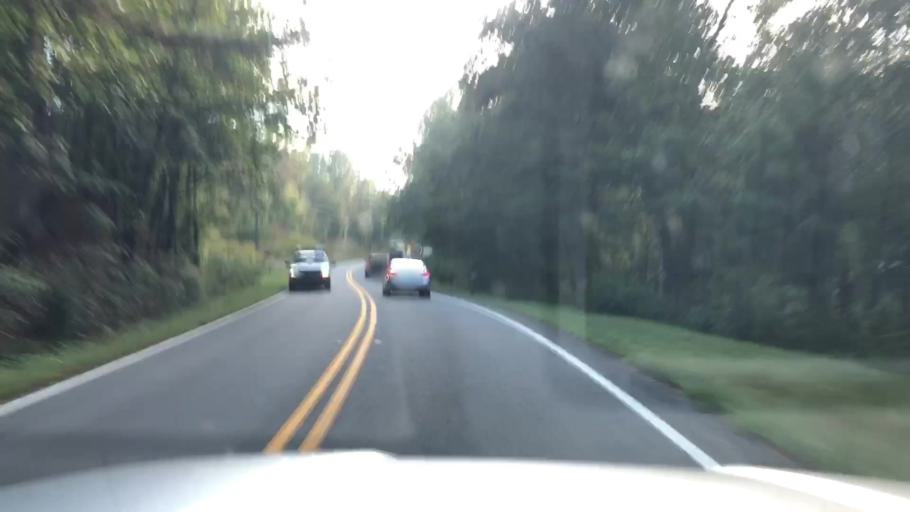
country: US
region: Georgia
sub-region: Bartow County
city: Emerson
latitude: 34.0792
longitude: -84.7670
